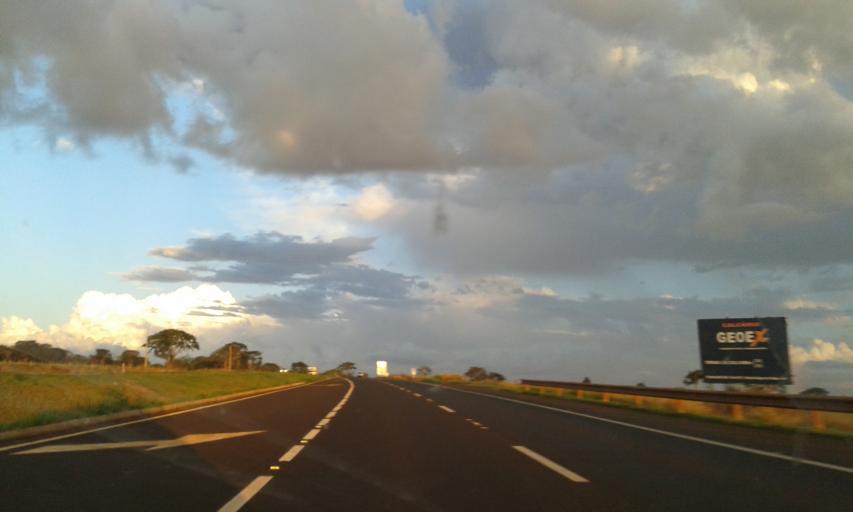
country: BR
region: Minas Gerais
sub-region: Monte Alegre De Minas
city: Monte Alegre de Minas
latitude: -18.8738
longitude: -48.7517
